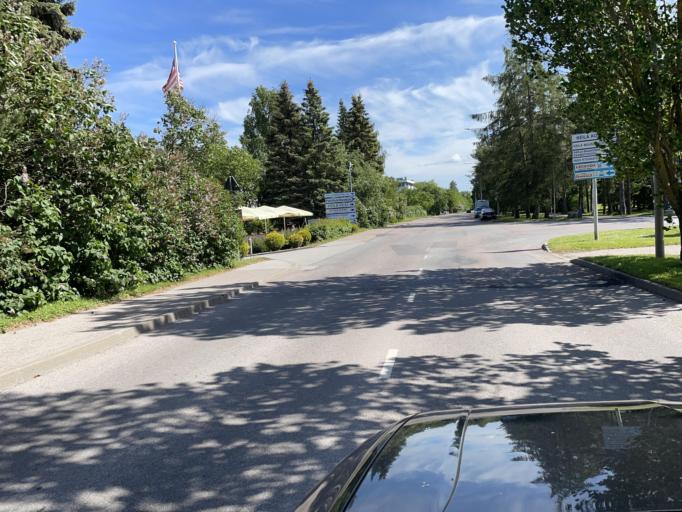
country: EE
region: Harju
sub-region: Keila linn
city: Keila
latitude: 59.3144
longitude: 24.4131
